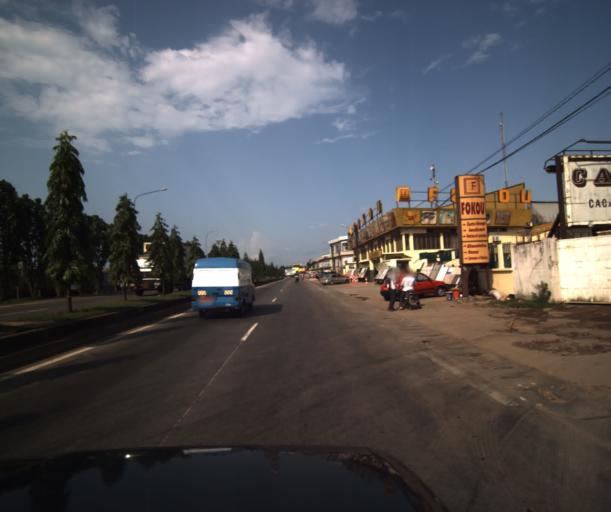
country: CM
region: Littoral
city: Douala
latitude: 4.0594
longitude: 9.6991
